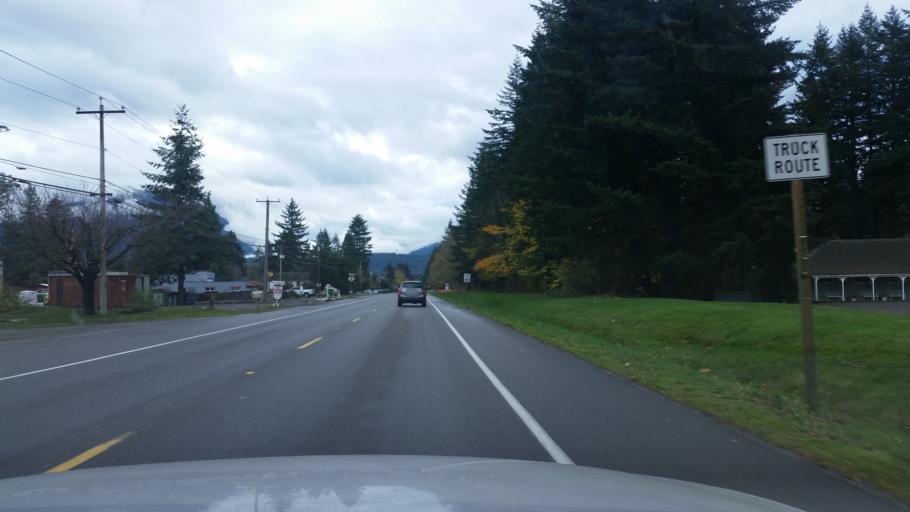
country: US
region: Washington
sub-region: King County
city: Tanner
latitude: 47.4839
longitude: -121.7635
